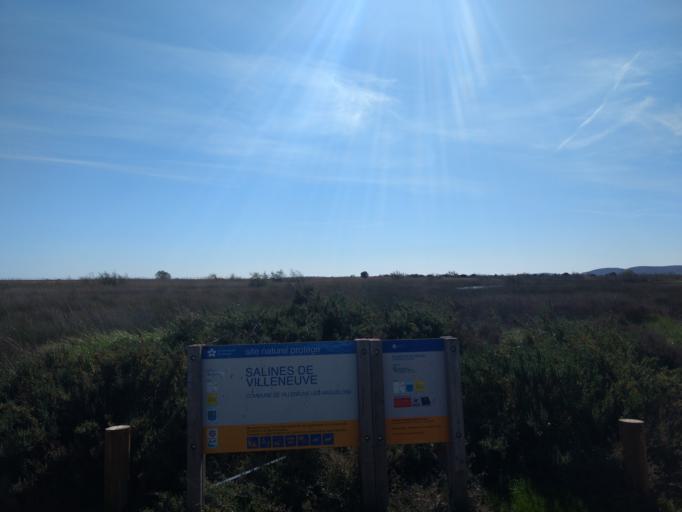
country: FR
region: Languedoc-Roussillon
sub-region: Departement de l'Herault
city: Mireval
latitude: 43.5152
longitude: 3.8337
